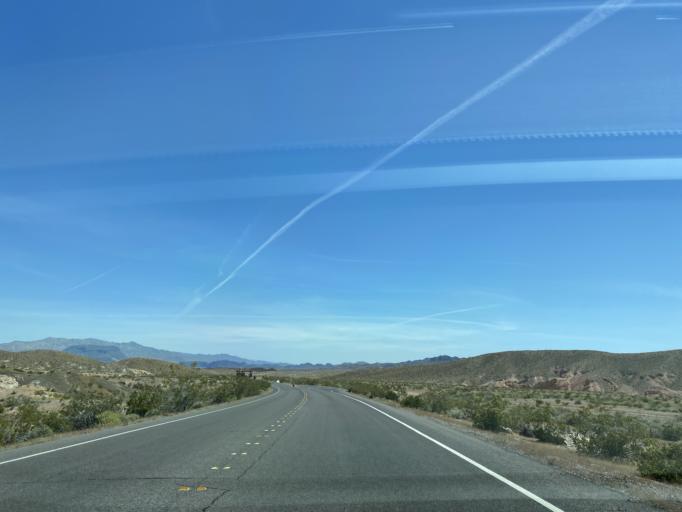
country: US
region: Nevada
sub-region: Clark County
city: Henderson
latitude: 36.1640
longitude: -114.9086
